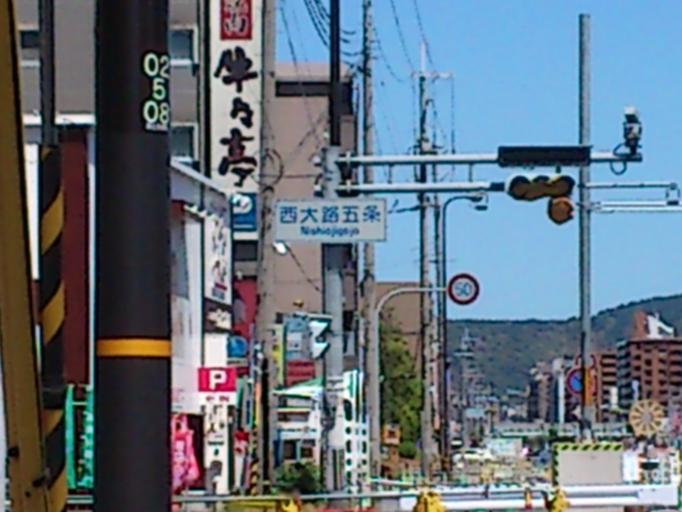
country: JP
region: Kyoto
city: Kyoto
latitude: 34.9968
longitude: 135.7319
